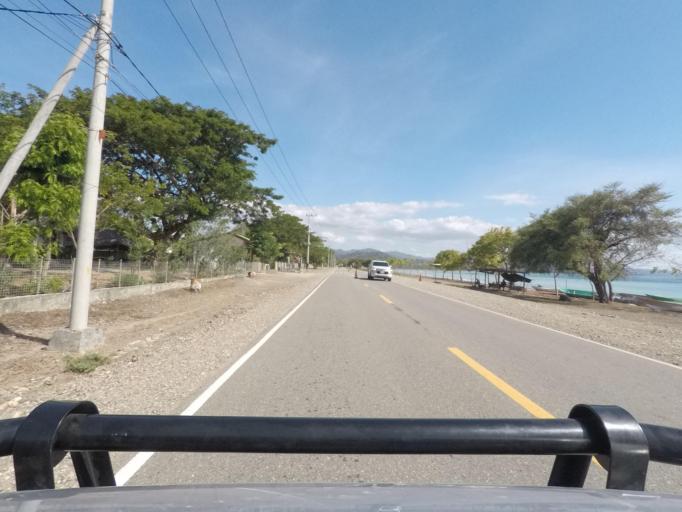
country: ID
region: East Nusa Tenggara
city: Atambua
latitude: -8.9322
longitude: 124.9807
